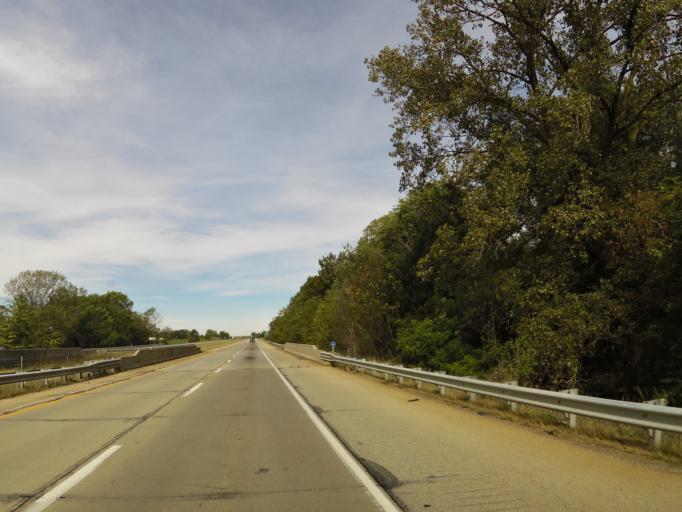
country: US
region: Indiana
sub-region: Hendricks County
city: Pittsboro
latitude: 39.9294
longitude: -86.5934
